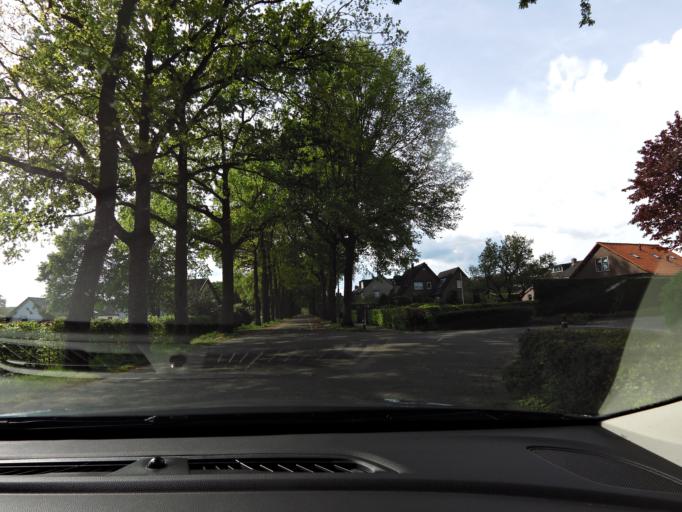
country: NL
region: Utrecht
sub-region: Gemeente Utrechtse Heuvelrug
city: Leersum
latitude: 52.0097
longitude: 5.4191
